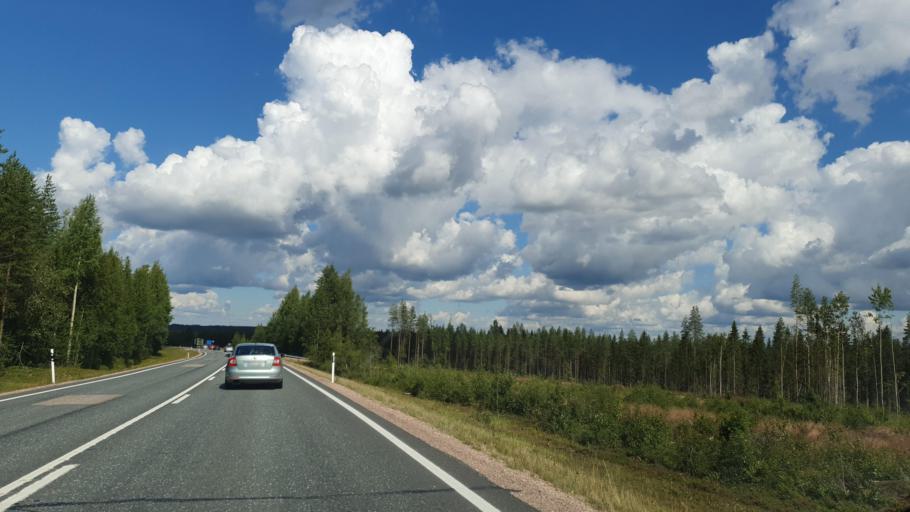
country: FI
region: Kainuu
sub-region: Kajaani
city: Kajaani
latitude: 64.0578
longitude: 27.4551
